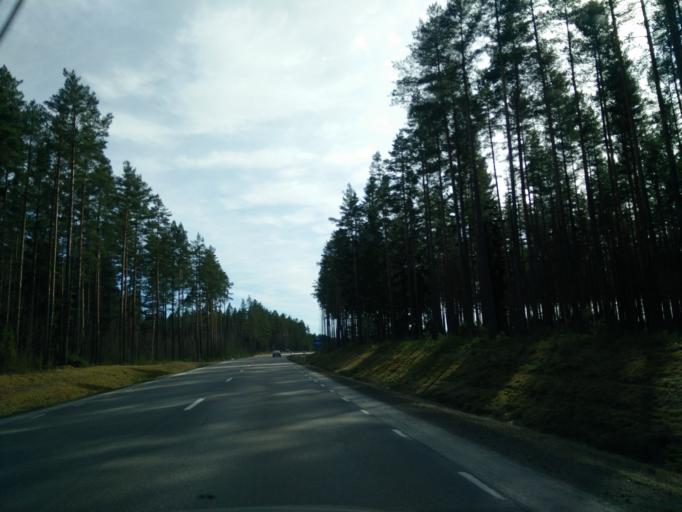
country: SE
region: Vaermland
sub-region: Hagfors Kommun
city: Hagfors
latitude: 60.0303
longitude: 13.5892
